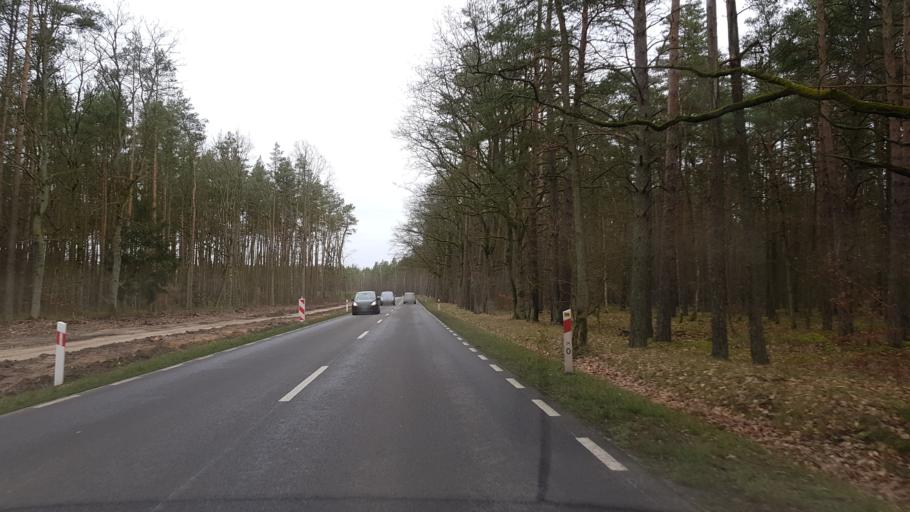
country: PL
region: West Pomeranian Voivodeship
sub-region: Powiat policki
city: Police
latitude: 53.6342
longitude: 14.5041
